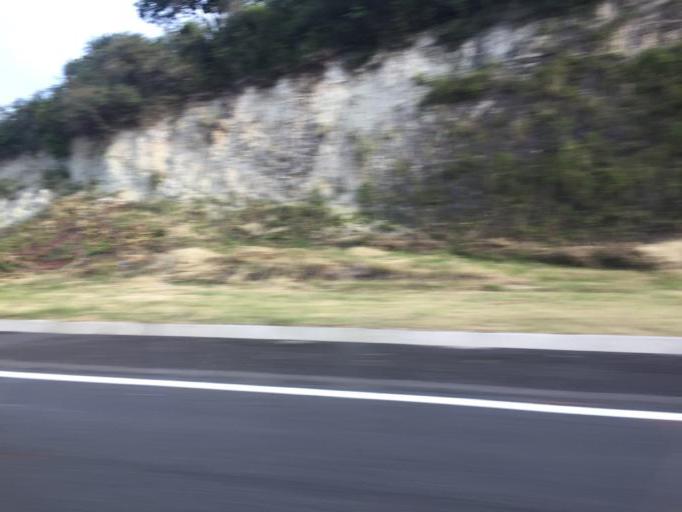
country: MX
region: Michoacan
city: Copandaro de Galeana
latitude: 19.8878
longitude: -101.1819
